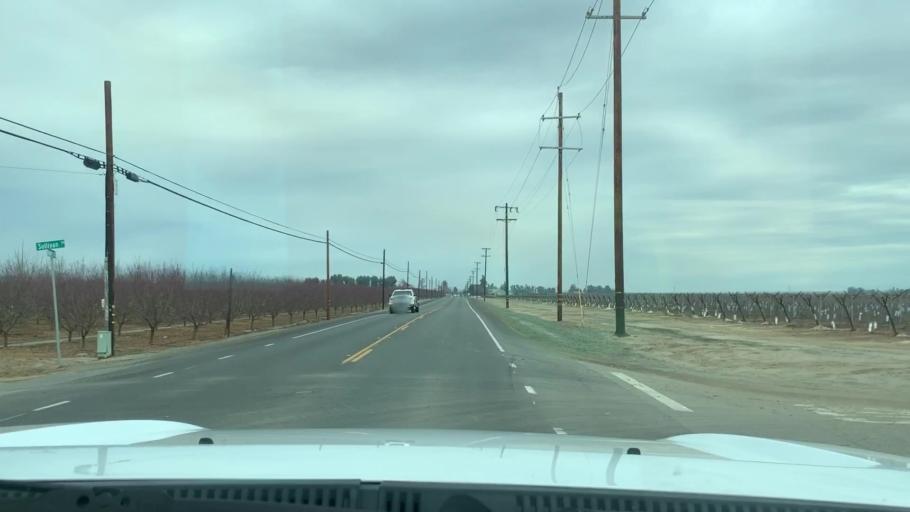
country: US
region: California
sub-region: Kern County
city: Shafter
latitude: 35.4127
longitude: -119.2519
